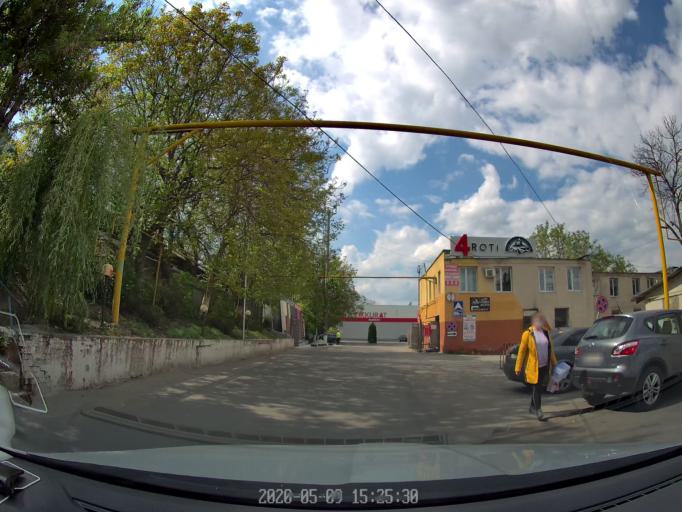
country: MD
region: Chisinau
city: Chisinau
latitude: 46.9783
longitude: 28.8798
